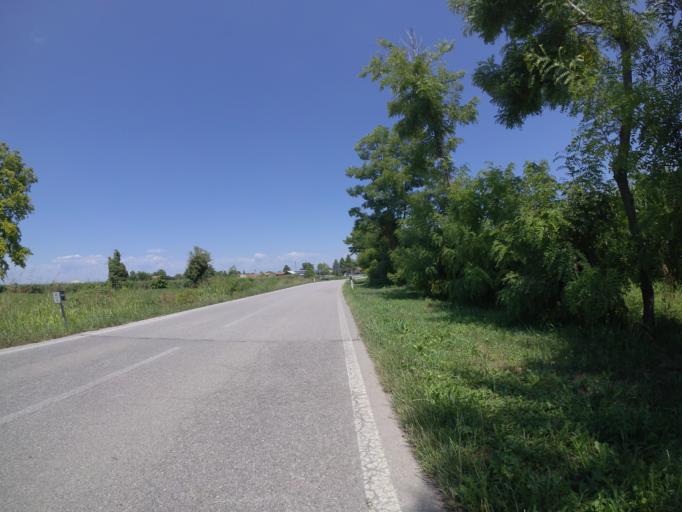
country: IT
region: Friuli Venezia Giulia
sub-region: Provincia di Udine
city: Talmassons
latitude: 45.9164
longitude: 13.1394
